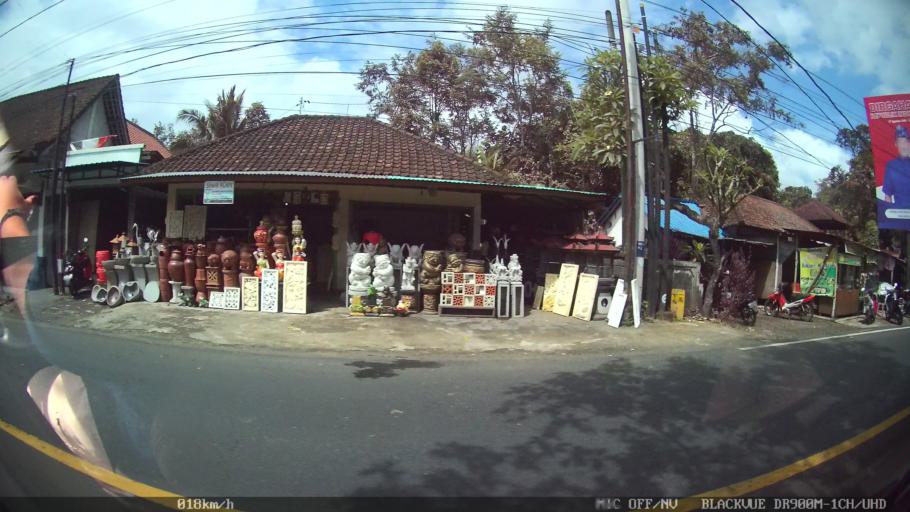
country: ID
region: Bali
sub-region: Kabupaten Gianyar
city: Ubud
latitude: -8.5236
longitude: 115.2882
